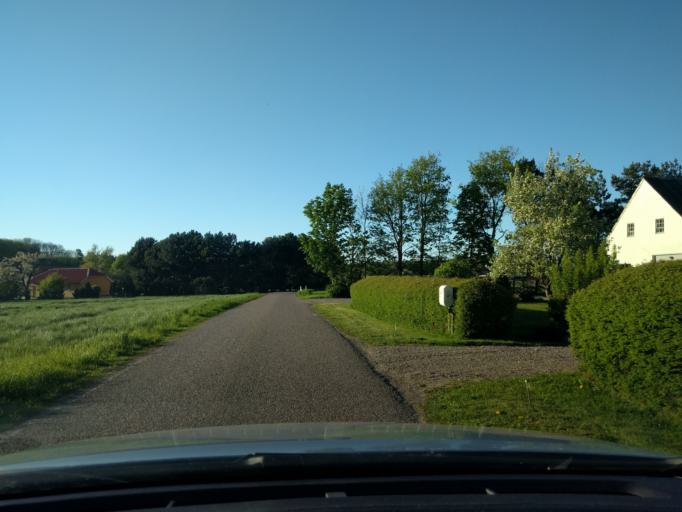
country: DK
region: South Denmark
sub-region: Nyborg Kommune
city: Ullerslev
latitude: 55.3981
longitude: 10.6481
